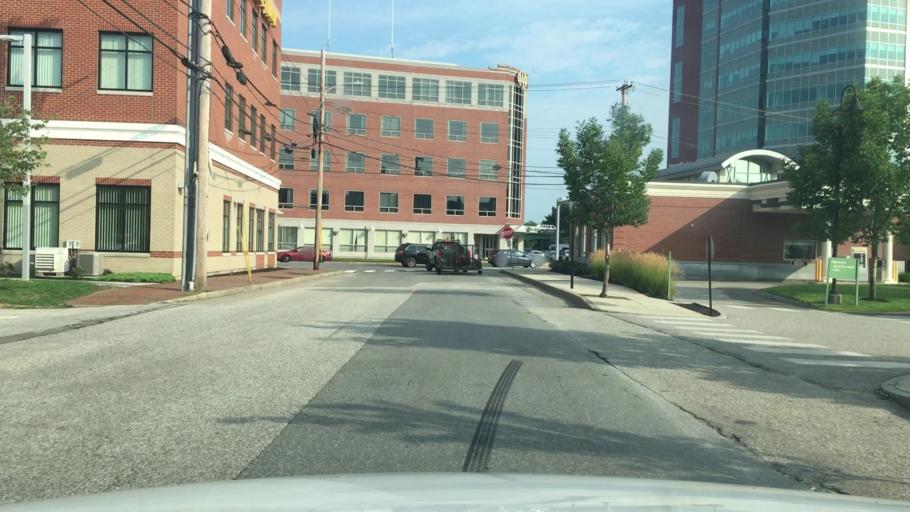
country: US
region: Maine
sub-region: Cumberland County
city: Portland
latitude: 43.6611
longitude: -70.2653
